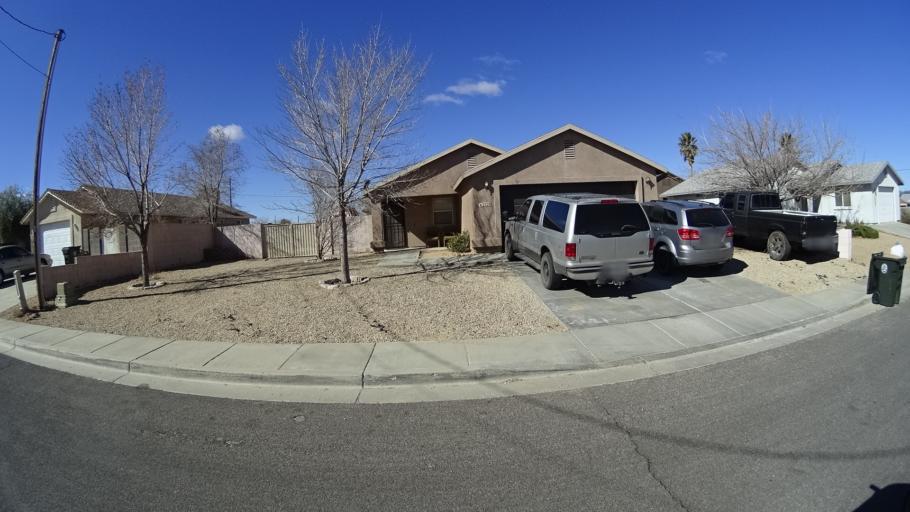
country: US
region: Arizona
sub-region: Mohave County
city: New Kingman-Butler
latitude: 35.2204
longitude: -113.9985
